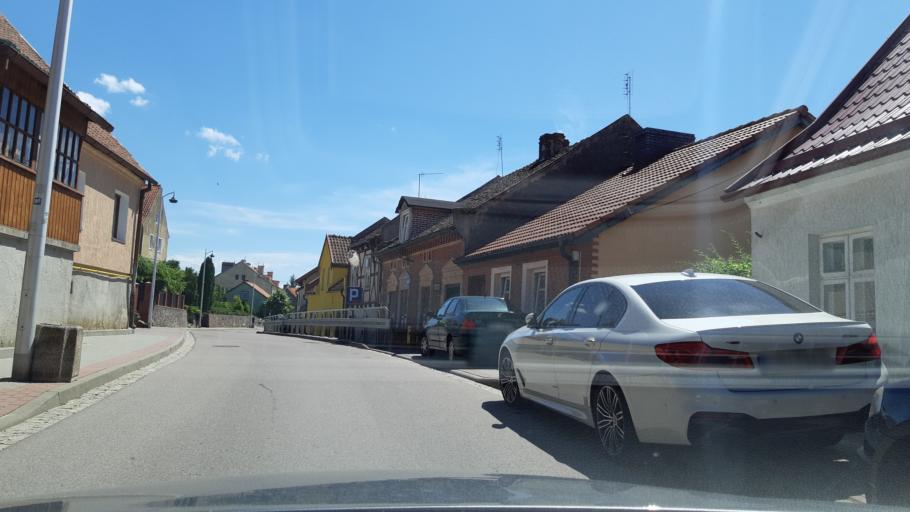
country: PL
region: Warmian-Masurian Voivodeship
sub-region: Powiat mragowski
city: Mikolajki
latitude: 53.7987
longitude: 21.5759
